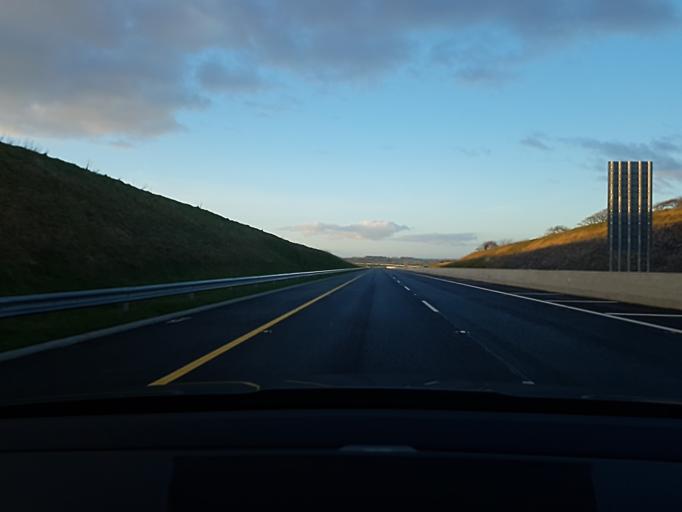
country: IE
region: Connaught
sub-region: County Galway
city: Tuam
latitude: 53.4105
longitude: -8.8267
